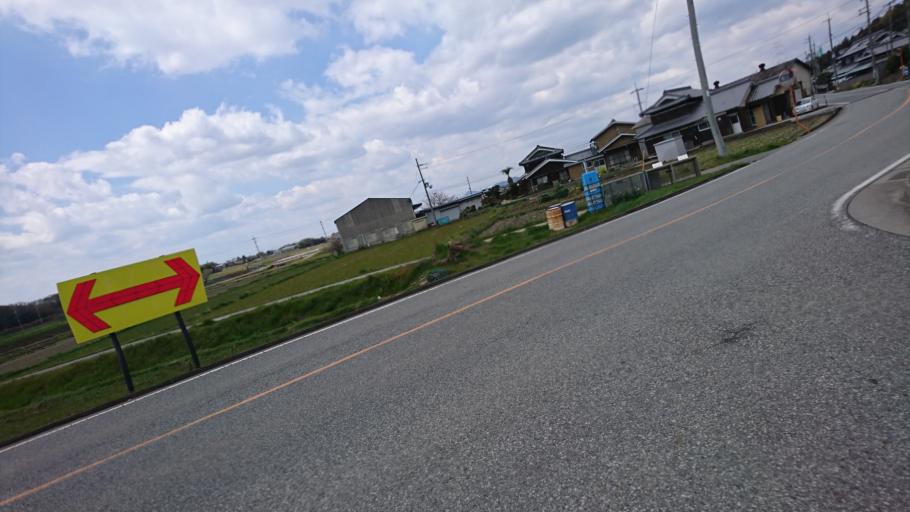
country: JP
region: Hyogo
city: Miki
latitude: 34.7692
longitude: 134.9495
